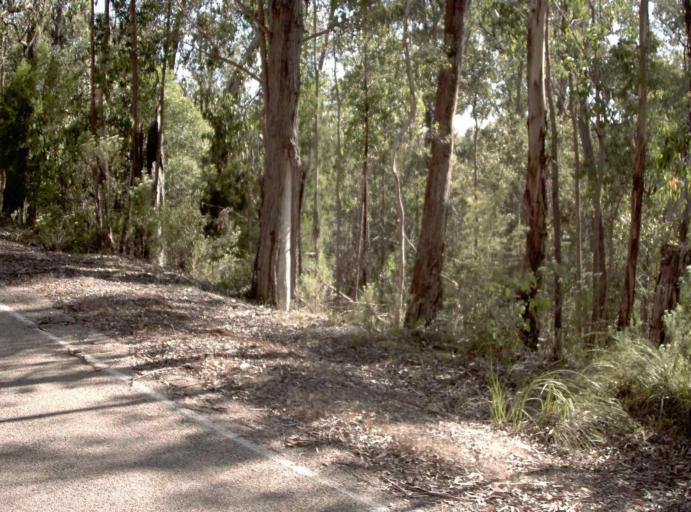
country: AU
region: Victoria
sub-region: East Gippsland
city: Lakes Entrance
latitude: -37.5538
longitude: 148.5598
